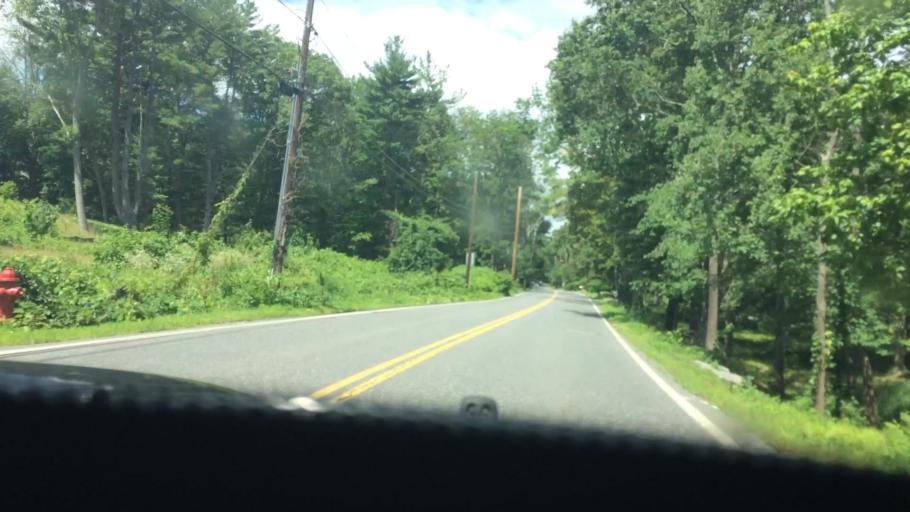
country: US
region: Massachusetts
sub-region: Middlesex County
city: Sudbury
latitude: 42.3783
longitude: -71.4044
